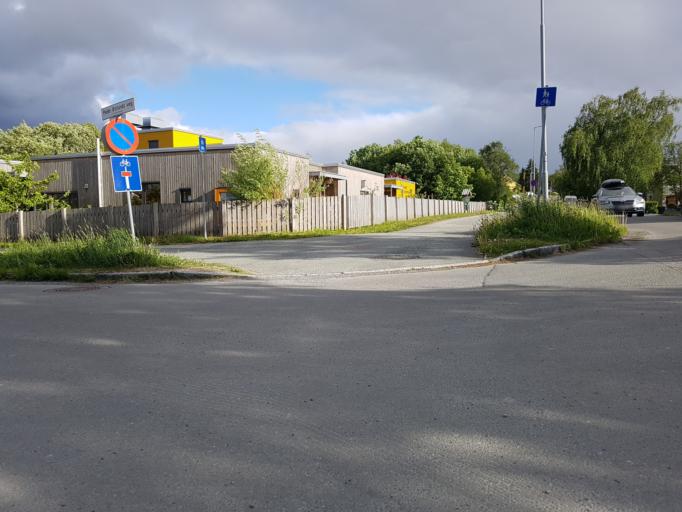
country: NO
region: Sor-Trondelag
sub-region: Trondheim
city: Trondheim
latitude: 63.4293
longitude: 10.4604
